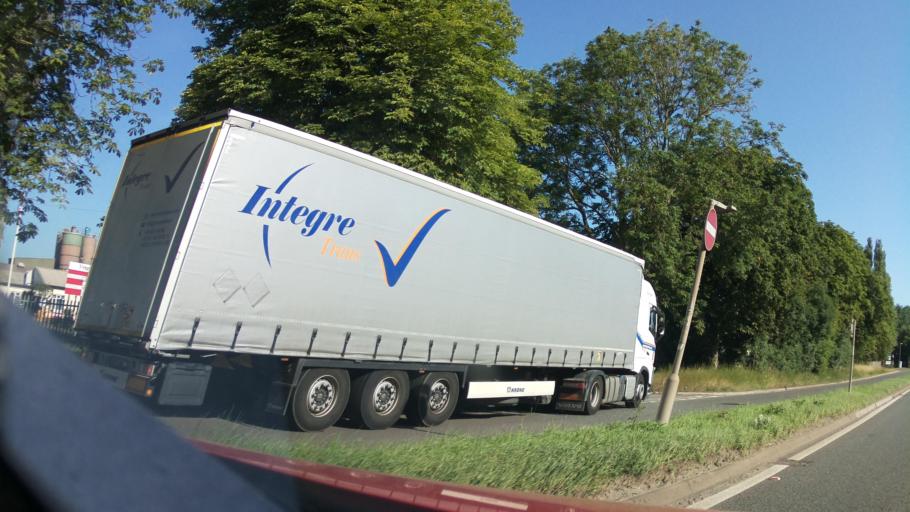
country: GB
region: England
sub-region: Staffordshire
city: Barton under Needwood
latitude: 52.7788
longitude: -1.6822
